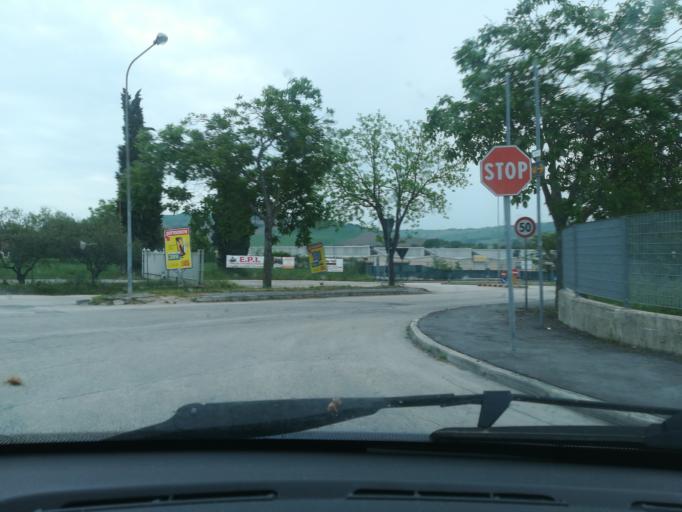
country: IT
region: The Marches
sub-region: Provincia di Macerata
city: San Severino Marche
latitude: 43.2402
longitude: 13.2202
